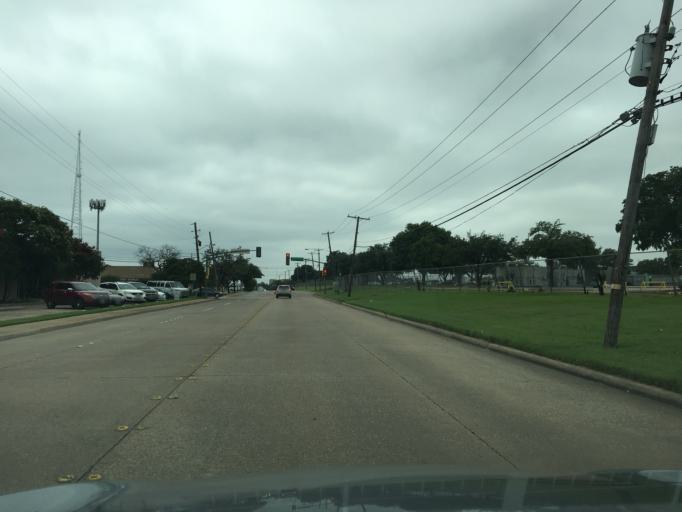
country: US
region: Texas
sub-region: Dallas County
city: Richardson
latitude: 32.9349
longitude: -96.7483
